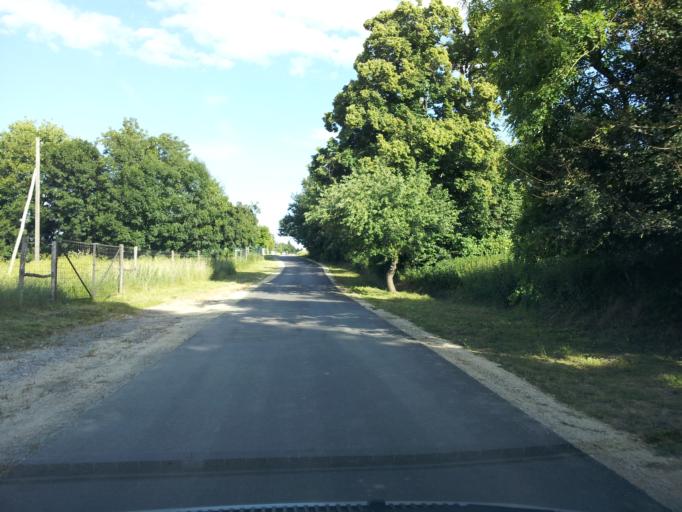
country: HU
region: Veszprem
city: Zirc
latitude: 47.2050
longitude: 17.8489
